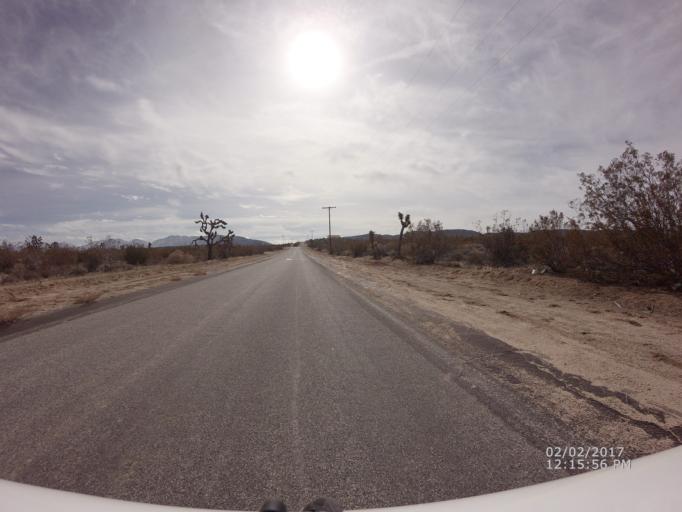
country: US
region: California
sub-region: Los Angeles County
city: Littlerock
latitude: 34.5093
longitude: -117.9749
